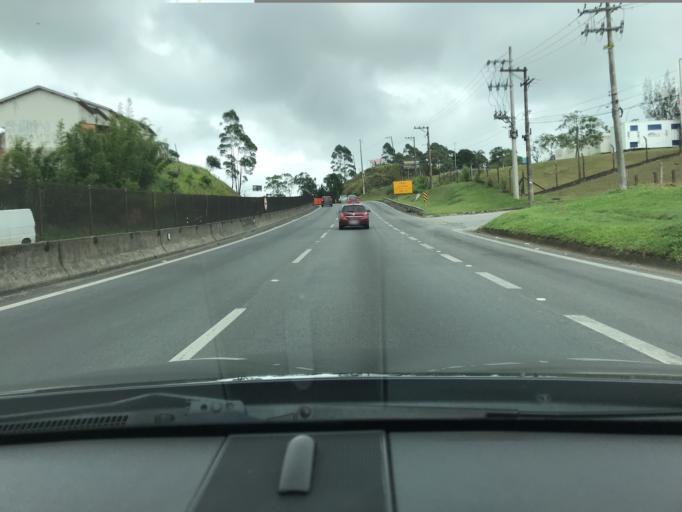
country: BR
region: Sao Paulo
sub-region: Cotia
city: Cotia
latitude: -23.6091
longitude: -46.9534
